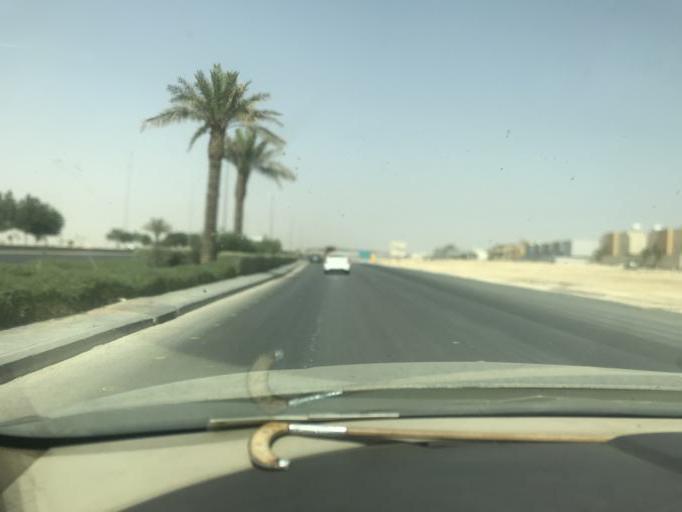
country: SA
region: Ar Riyad
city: Riyadh
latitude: 24.8389
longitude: 46.6443
